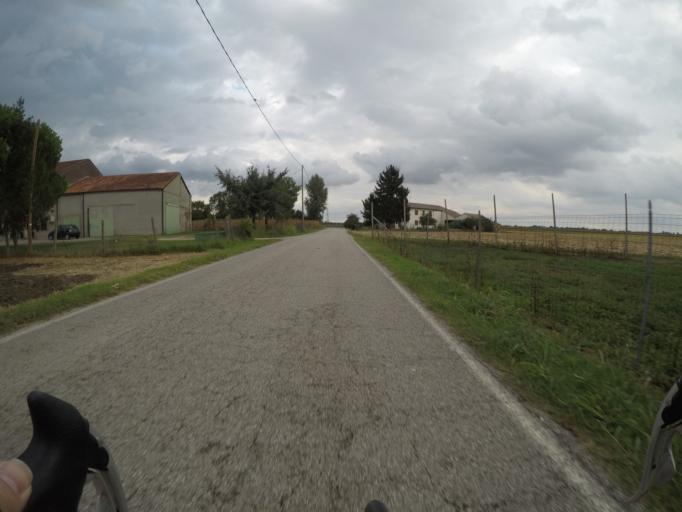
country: IT
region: Veneto
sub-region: Provincia di Rovigo
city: Frassinelle Polesine
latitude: 44.9855
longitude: 11.7251
